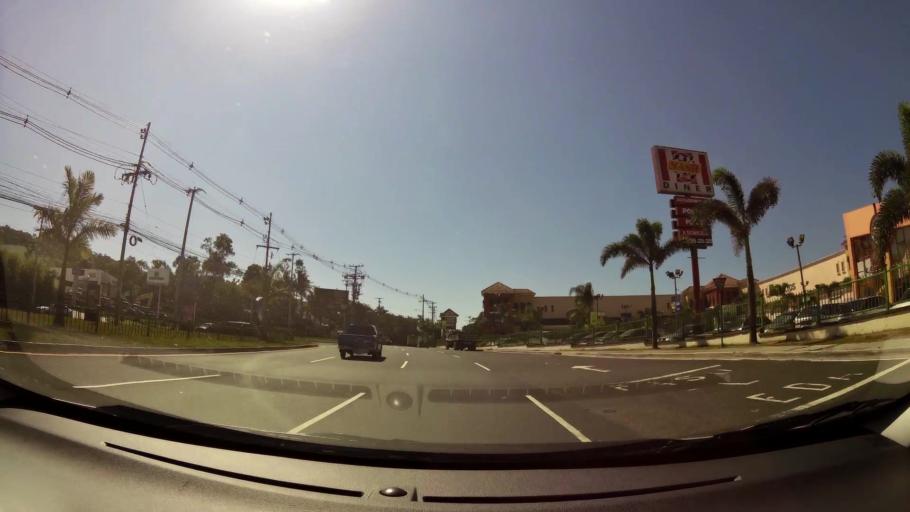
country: SV
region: La Libertad
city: Nuevo Cuscatlan
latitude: 13.6571
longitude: -89.2786
